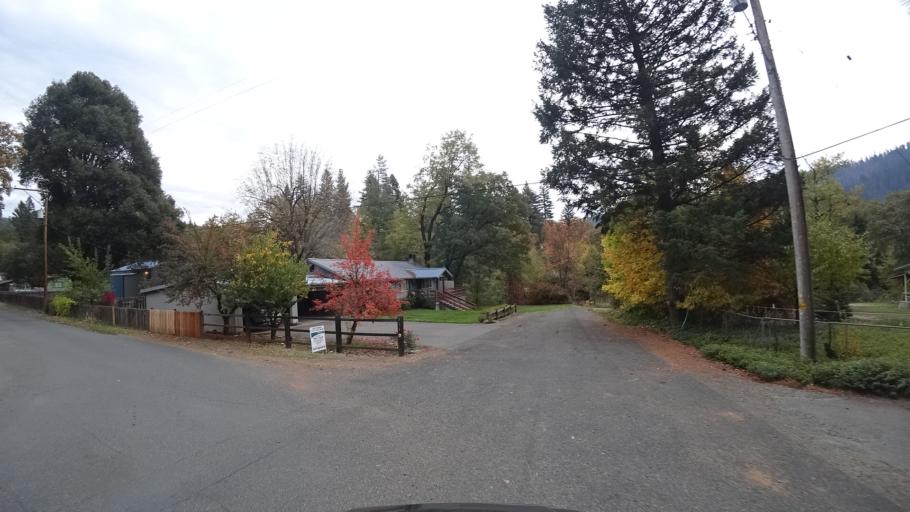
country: US
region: California
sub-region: Siskiyou County
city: Happy Camp
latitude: 41.7969
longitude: -123.3798
